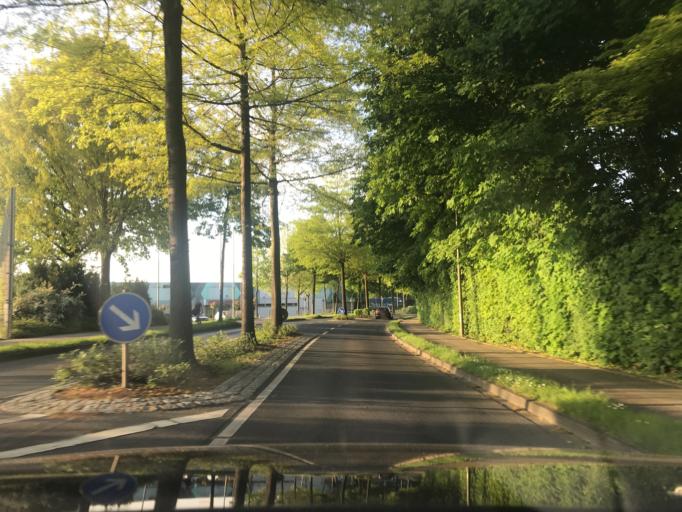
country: DE
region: North Rhine-Westphalia
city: Erkelenz
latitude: 51.0797
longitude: 6.3089
